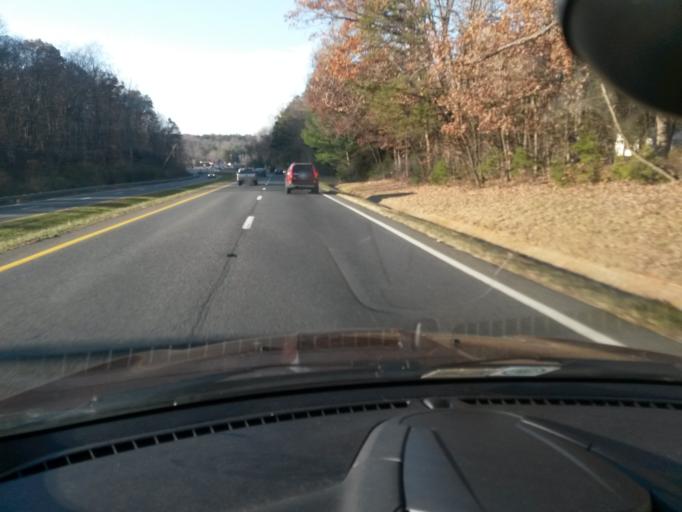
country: US
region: Virginia
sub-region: Campbell County
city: Concord
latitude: 37.3678
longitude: -79.0133
